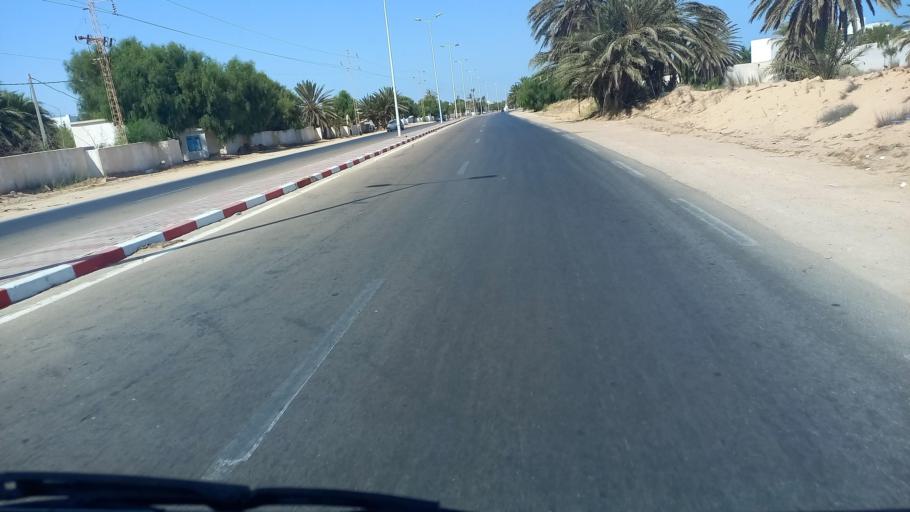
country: TN
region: Madanin
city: Midoun
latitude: 33.8265
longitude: 11.0366
